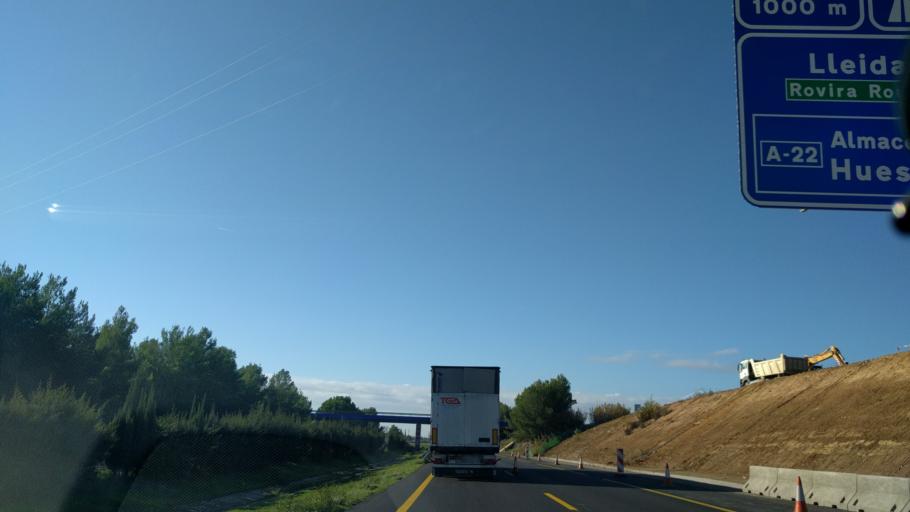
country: ES
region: Catalonia
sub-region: Provincia de Lleida
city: Alpicat
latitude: 41.6546
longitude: 0.5770
